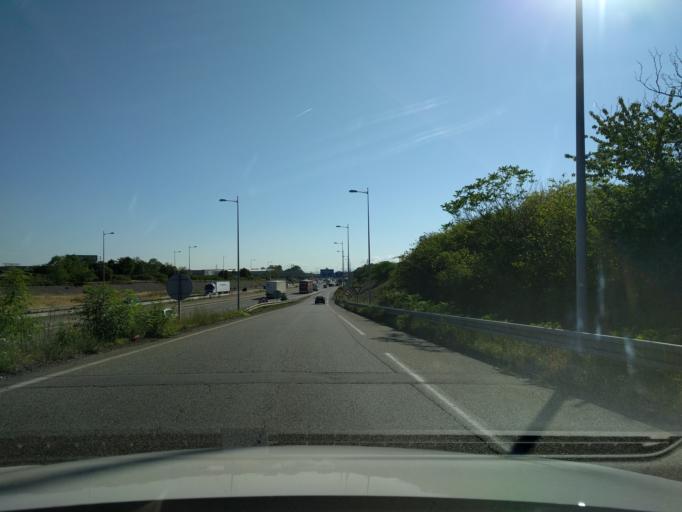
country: FR
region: Alsace
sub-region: Departement du Haut-Rhin
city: Sausheim
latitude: 47.7733
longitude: 7.3826
